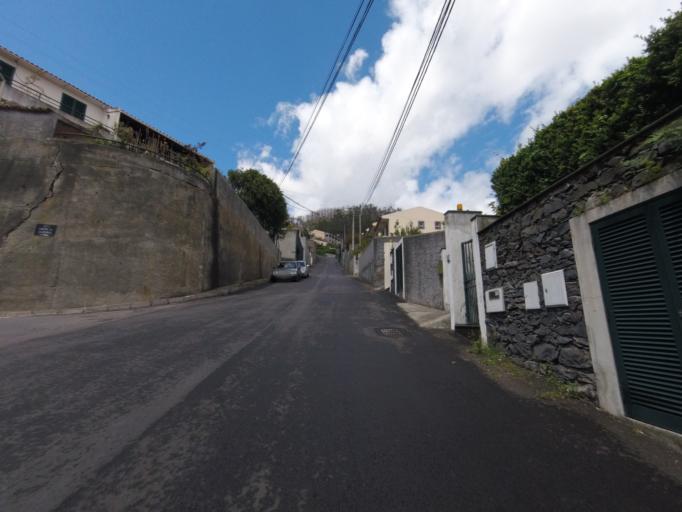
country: PT
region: Madeira
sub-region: Funchal
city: Nossa Senhora do Monte
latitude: 32.6781
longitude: -16.9203
